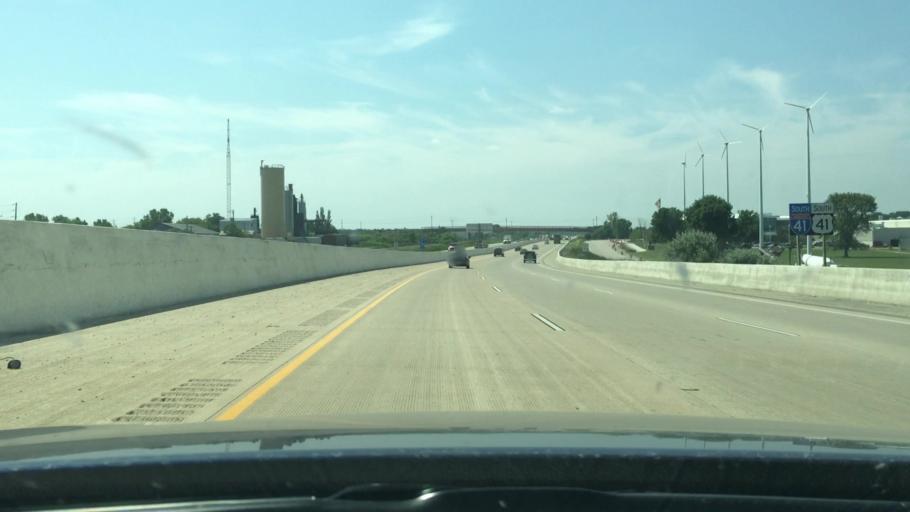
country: US
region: Wisconsin
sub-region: Winnebago County
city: Neenah
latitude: 44.1481
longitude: -88.4876
